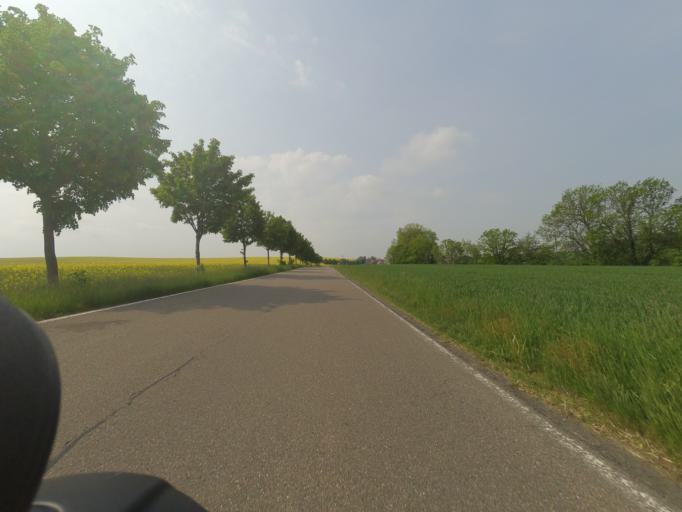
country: DE
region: Saxony
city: Obercunnersdorf
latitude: 50.8963
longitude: 13.5930
